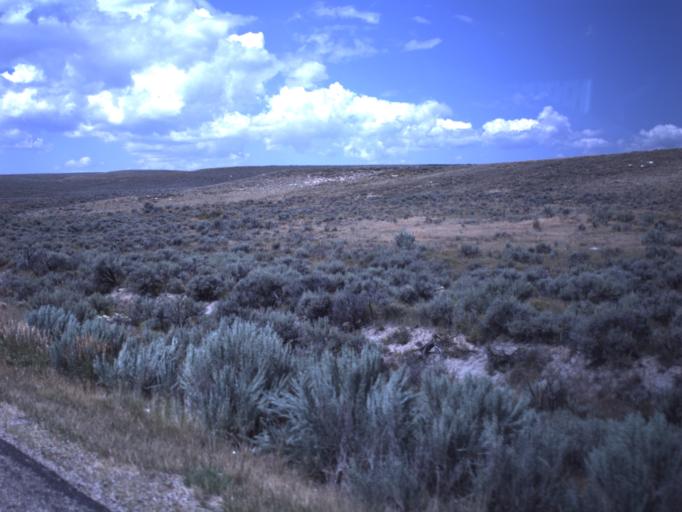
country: US
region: Utah
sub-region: Rich County
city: Randolph
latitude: 41.7709
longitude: -111.1395
